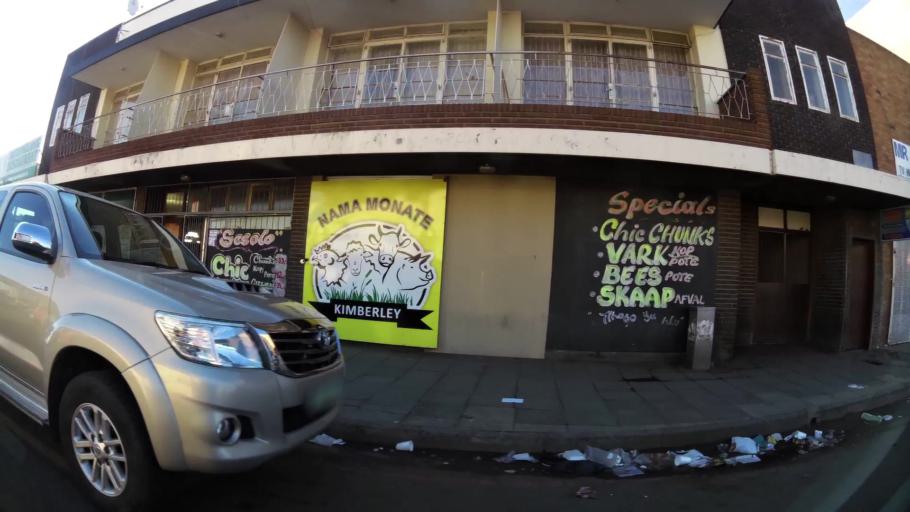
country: ZA
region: Northern Cape
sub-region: Frances Baard District Municipality
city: Kimberley
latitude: -28.7404
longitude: 24.7619
